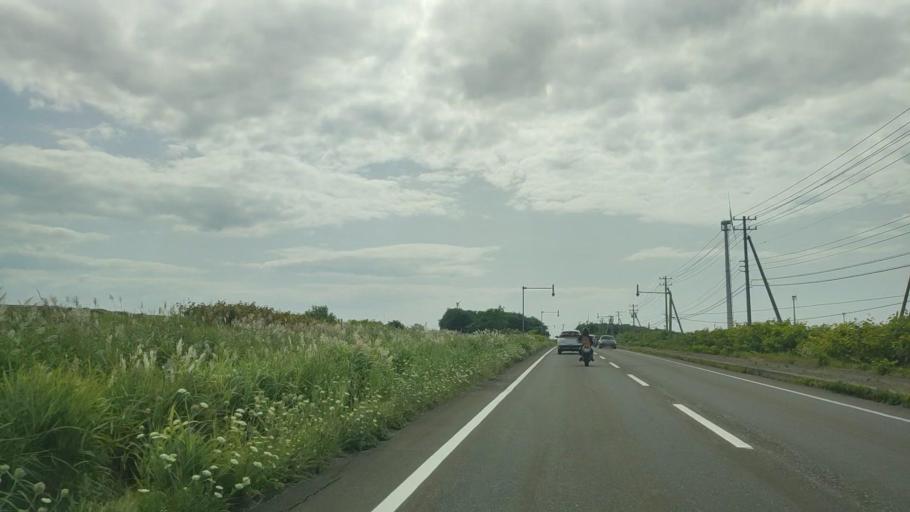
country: JP
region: Hokkaido
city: Rumoi
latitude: 44.3994
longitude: 141.7224
